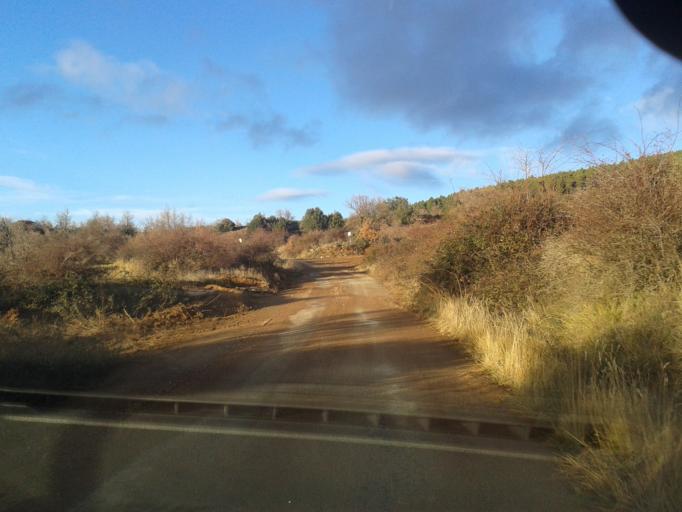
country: ES
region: Aragon
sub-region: Provincia de Teruel
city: Lagueruela
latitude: 41.0132
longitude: -1.1798
